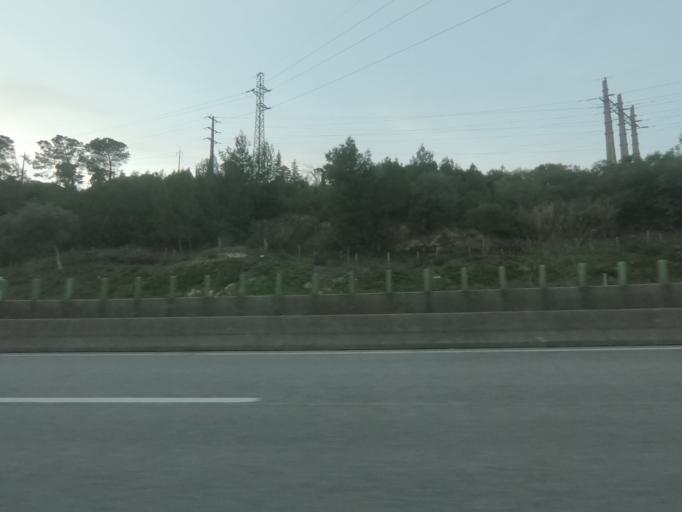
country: PT
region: Lisbon
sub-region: Vila Franca de Xira
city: Alhandra
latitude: 38.9219
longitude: -9.0157
